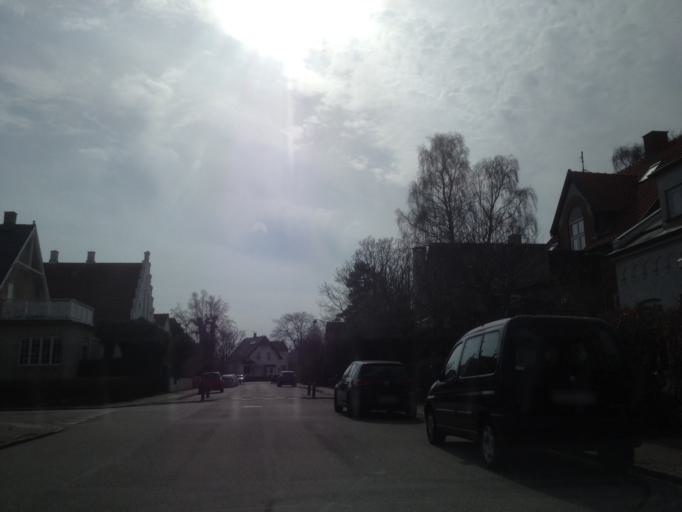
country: DK
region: Capital Region
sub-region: Gentofte Kommune
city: Charlottenlund
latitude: 55.7442
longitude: 12.5756
